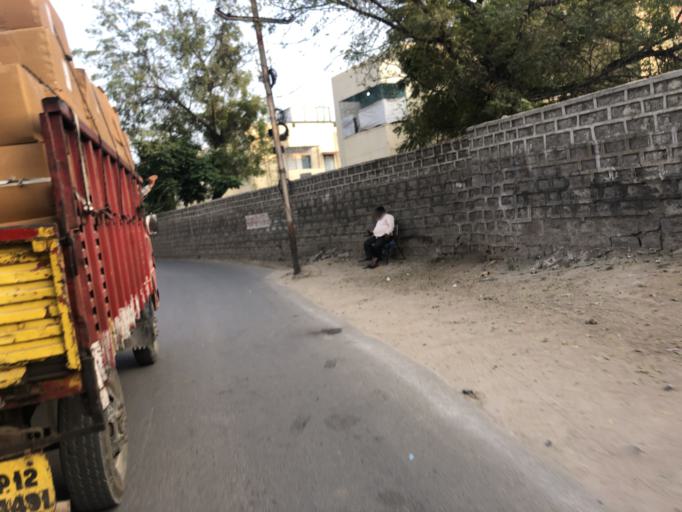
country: IN
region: Telangana
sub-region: Rangareddi
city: Kukatpalli
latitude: 17.4628
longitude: 78.4327
